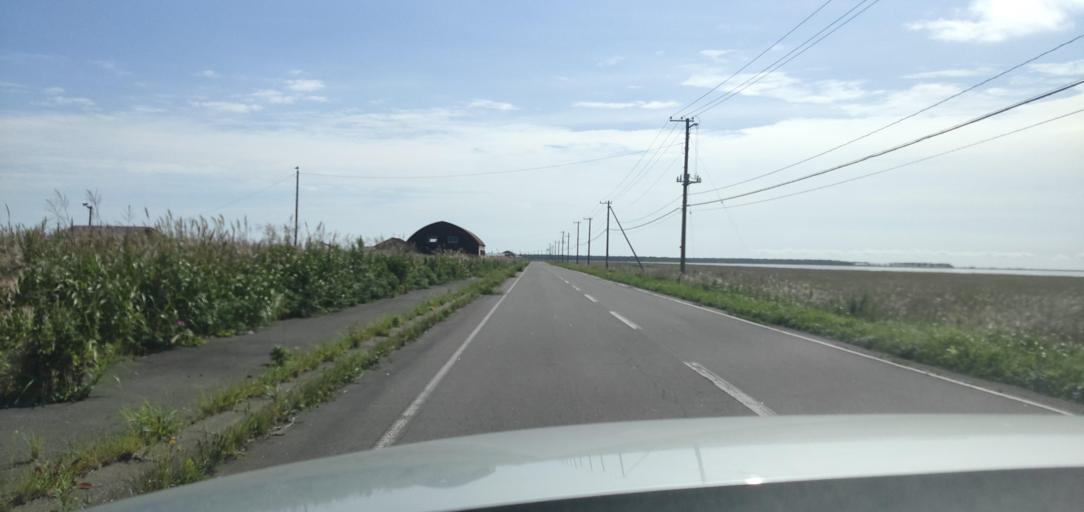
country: JP
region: Hokkaido
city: Shibetsu
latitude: 43.6180
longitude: 145.2337
